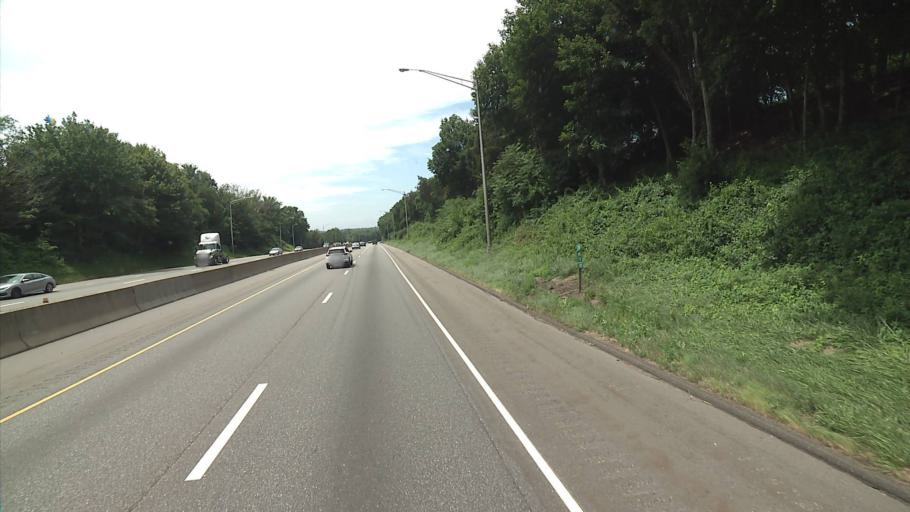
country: US
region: Connecticut
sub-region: New Haven County
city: Guilford Center
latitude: 41.2894
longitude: -72.6586
